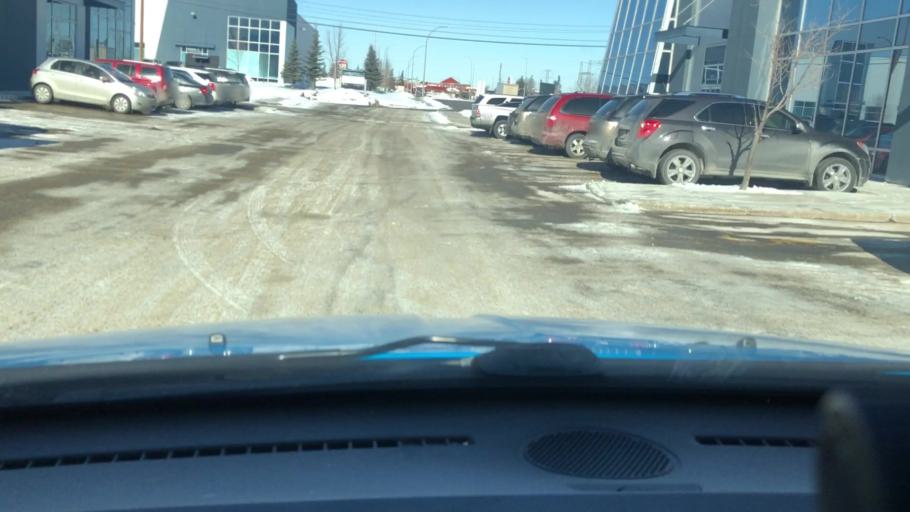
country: CA
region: Alberta
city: Calgary
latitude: 51.0061
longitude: -114.0043
